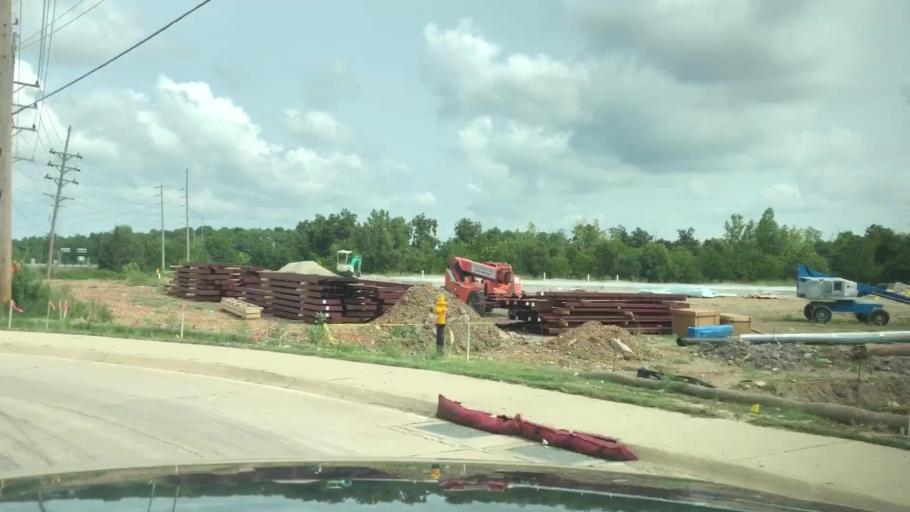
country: US
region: Missouri
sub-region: Saint Charles County
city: Wentzville
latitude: 38.8201
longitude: -90.8498
